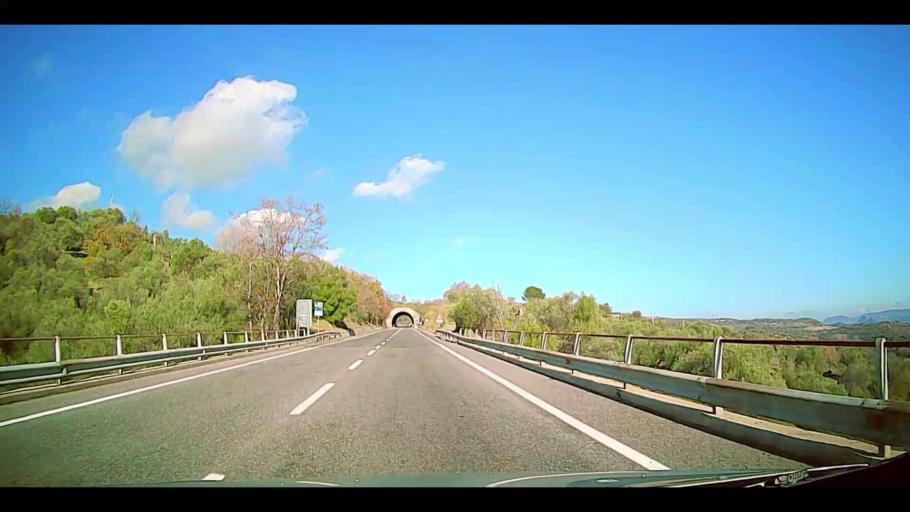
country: IT
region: Calabria
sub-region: Provincia di Crotone
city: Caccuri
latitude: 39.2174
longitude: 16.7962
